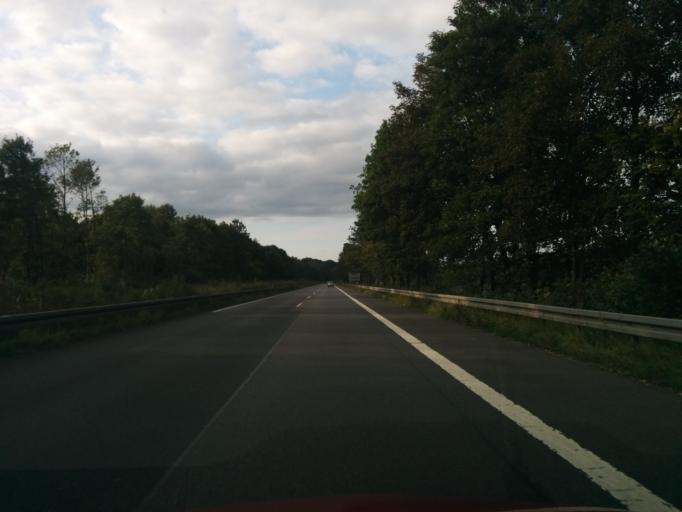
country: DE
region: Lower Saxony
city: Hoerden
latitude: 51.7002
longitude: 10.2843
